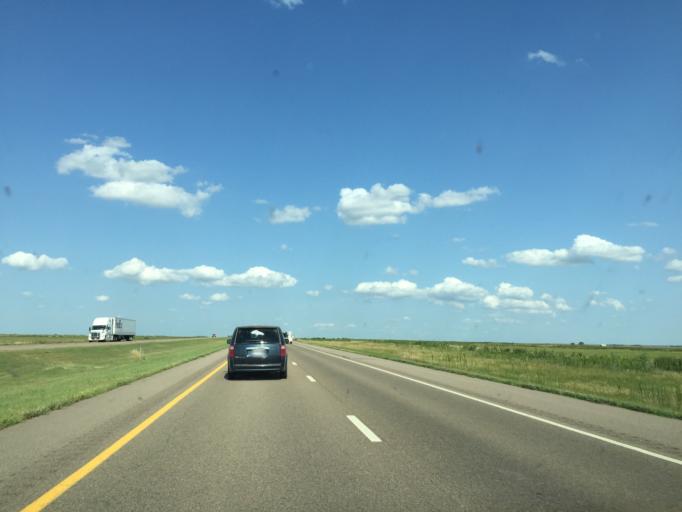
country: US
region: Kansas
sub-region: Trego County
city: WaKeeney
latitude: 39.0230
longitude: -99.9930
